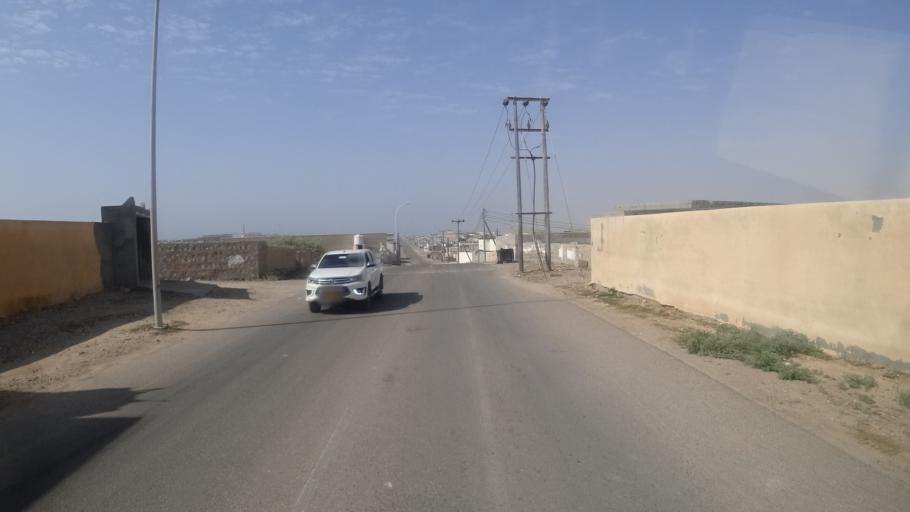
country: OM
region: Ash Sharqiyah
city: Sur
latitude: 22.1840
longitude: 59.7640
